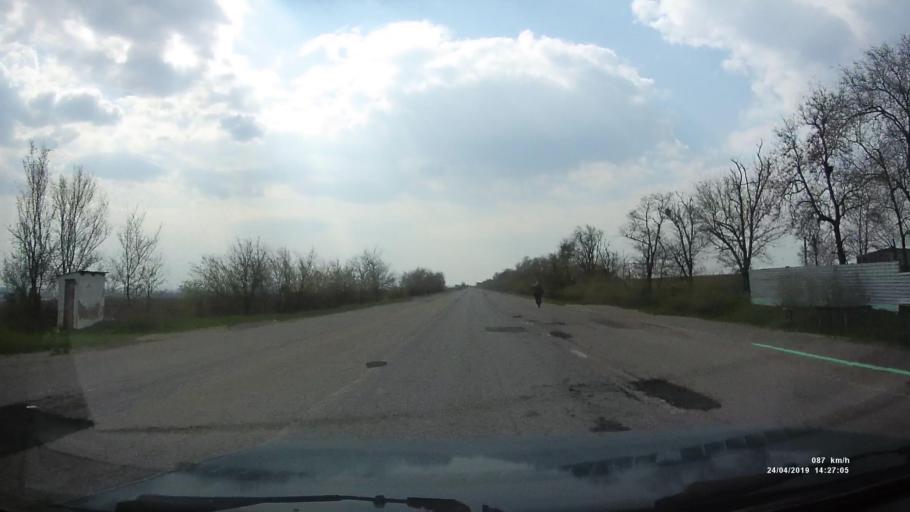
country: RU
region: Kalmykiya
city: Arshan'
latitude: 46.3341
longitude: 44.0496
